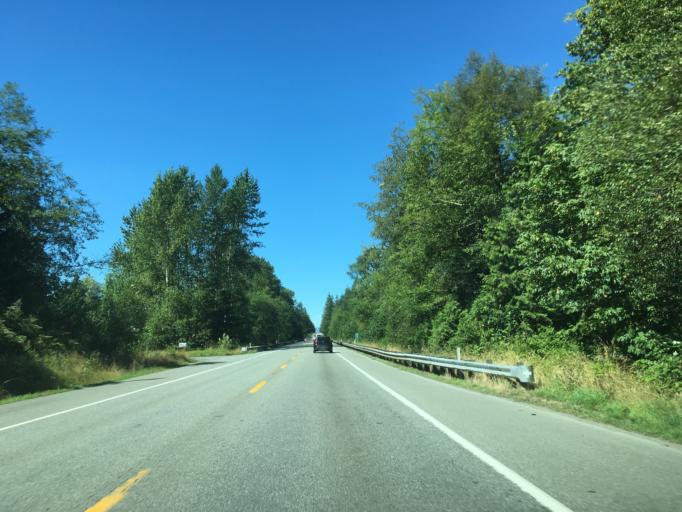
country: US
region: Washington
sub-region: Snohomish County
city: Sisco Heights
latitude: 48.0775
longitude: -122.1115
